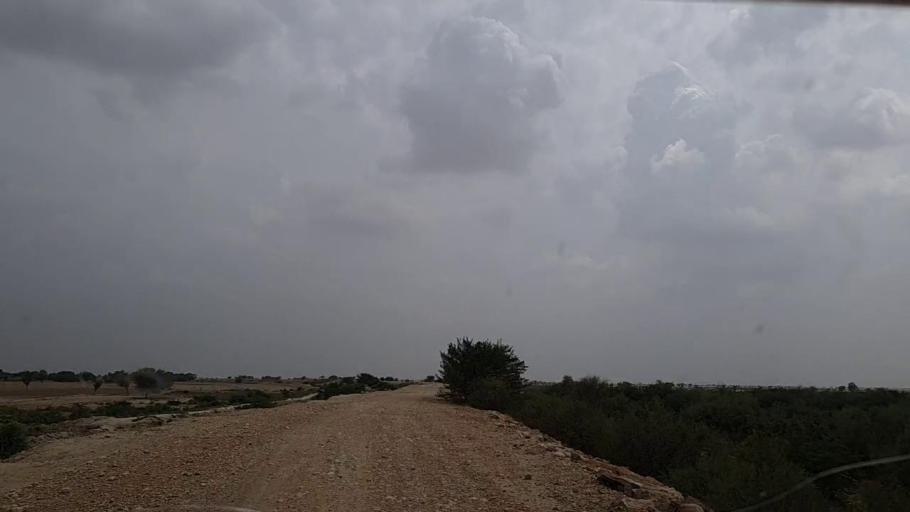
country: PK
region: Sindh
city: Johi
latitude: 26.7304
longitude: 67.5787
